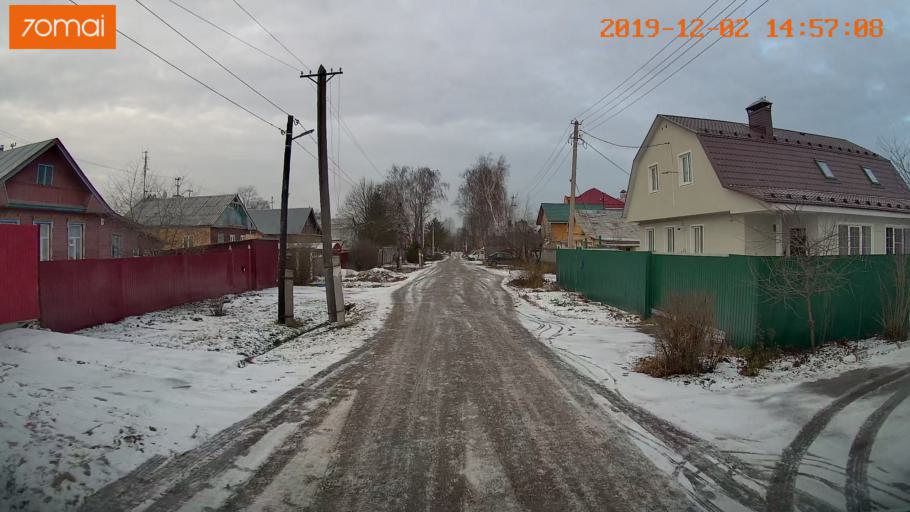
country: RU
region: Ivanovo
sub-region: Gorod Ivanovo
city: Ivanovo
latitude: 56.9736
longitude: 41.0141
